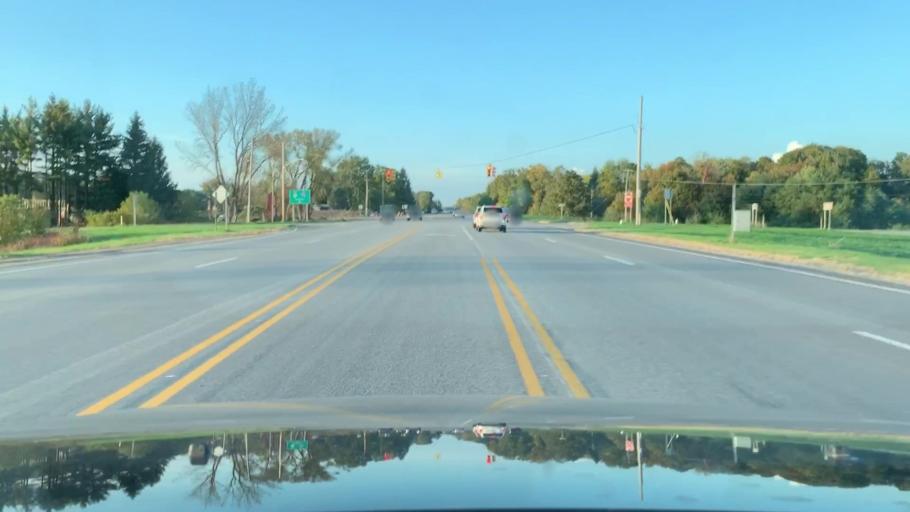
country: US
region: Michigan
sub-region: Ottawa County
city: Jenison
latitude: 42.8480
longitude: -85.8022
